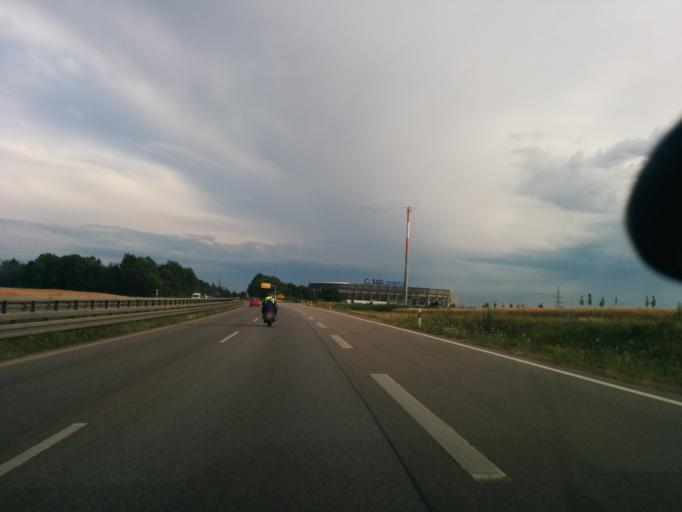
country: DE
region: Bavaria
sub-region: Swabia
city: Augsburg
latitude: 48.3291
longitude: 10.8868
